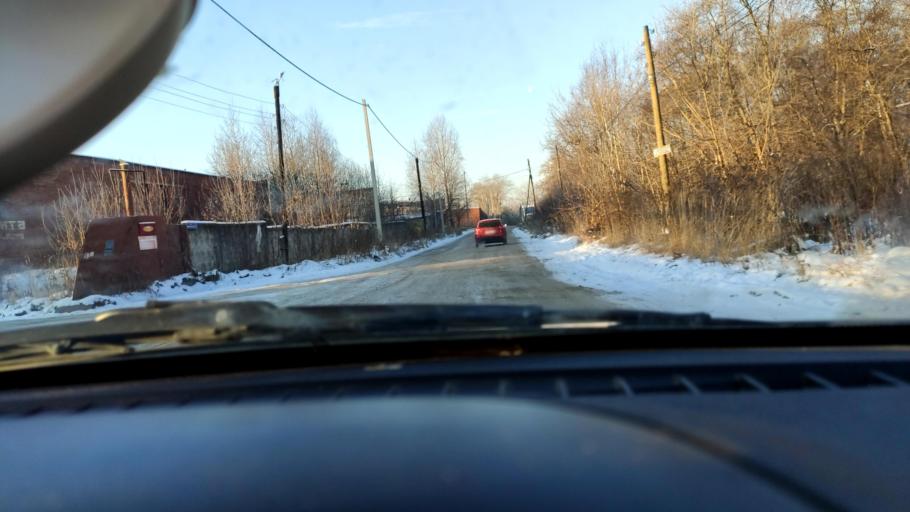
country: RU
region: Perm
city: Perm
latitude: 58.0714
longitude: 56.3617
